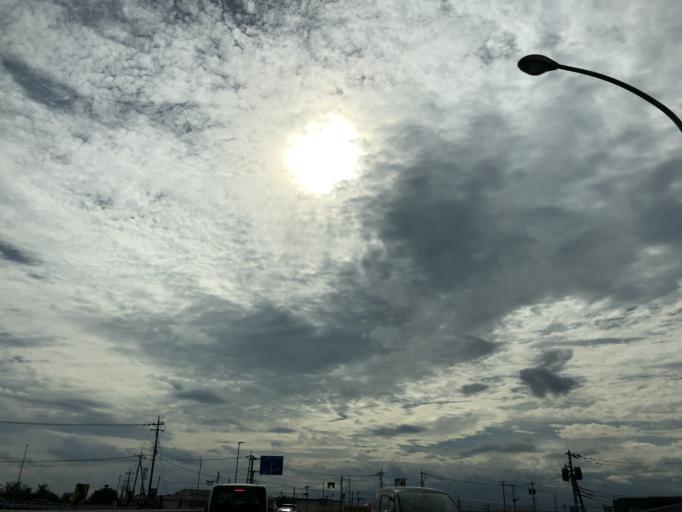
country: JP
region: Tochigi
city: Sano
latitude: 36.3006
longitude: 139.5703
